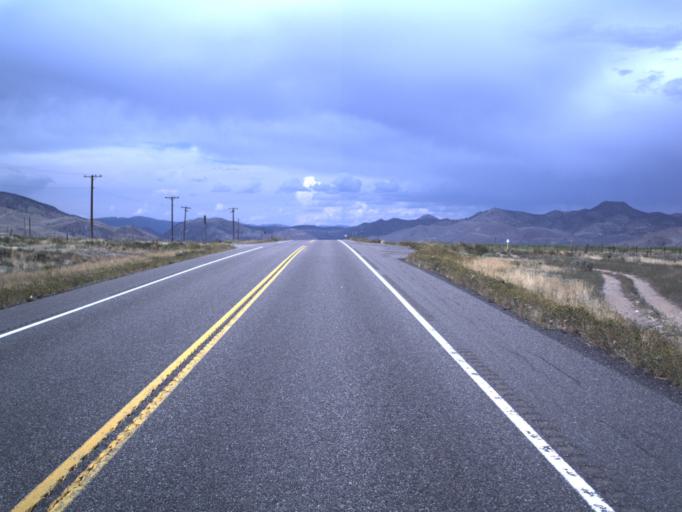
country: US
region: Utah
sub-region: Piute County
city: Junction
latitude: 38.4156
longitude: -112.2314
